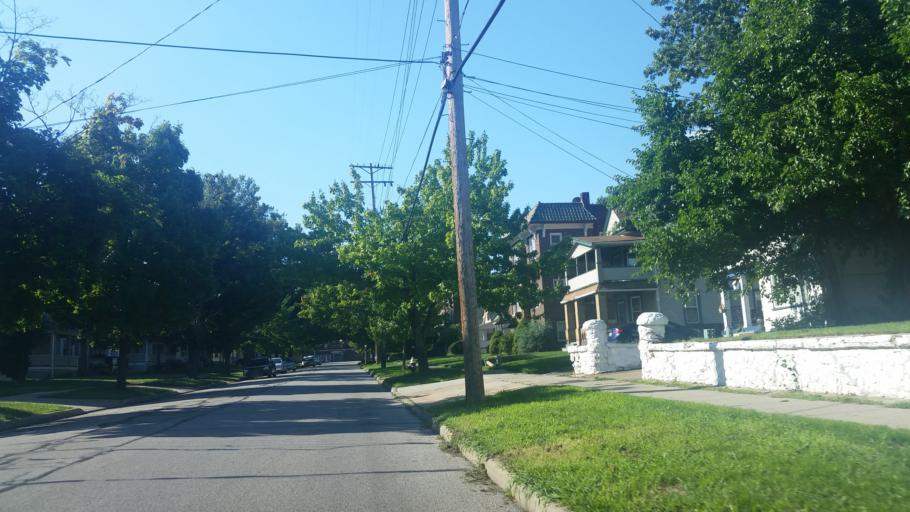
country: US
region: Ohio
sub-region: Cuyahoga County
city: Lakewood
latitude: 41.4862
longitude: -81.7754
